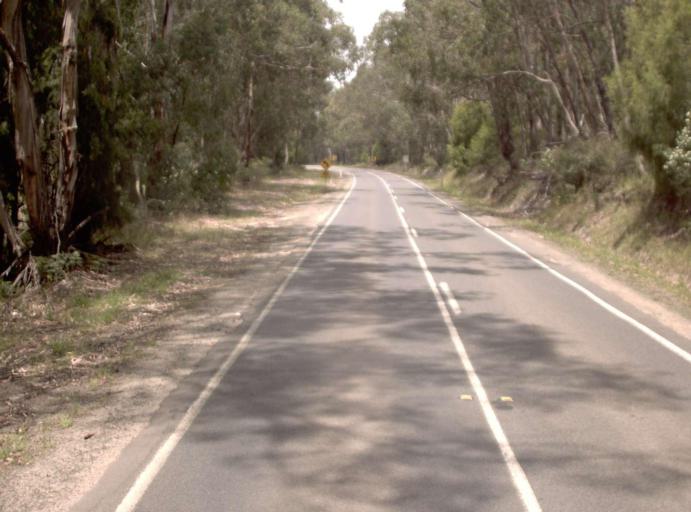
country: AU
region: Victoria
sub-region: Latrobe
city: Traralgon
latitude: -38.4027
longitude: 146.7498
